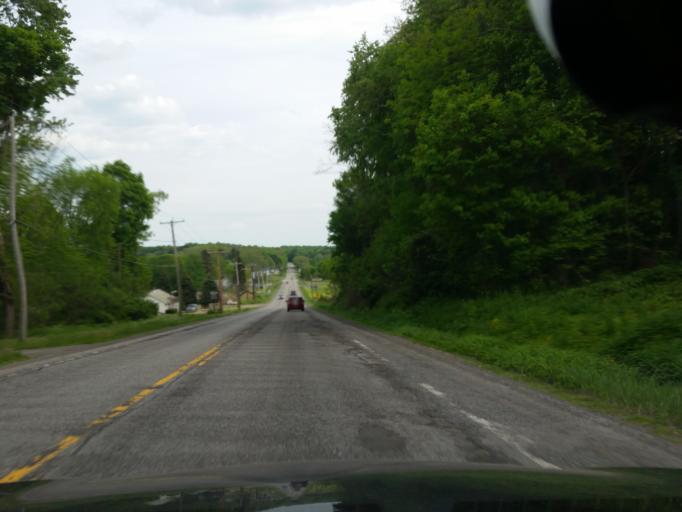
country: US
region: New York
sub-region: Chautauqua County
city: Mayville
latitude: 42.2059
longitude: -79.4228
